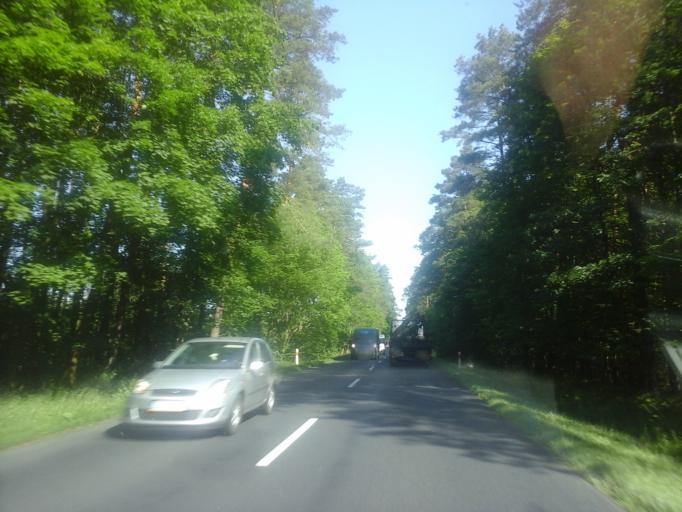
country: PL
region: West Pomeranian Voivodeship
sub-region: Powiat bialogardzki
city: Bialogard
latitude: 53.9597
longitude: 16.0548
